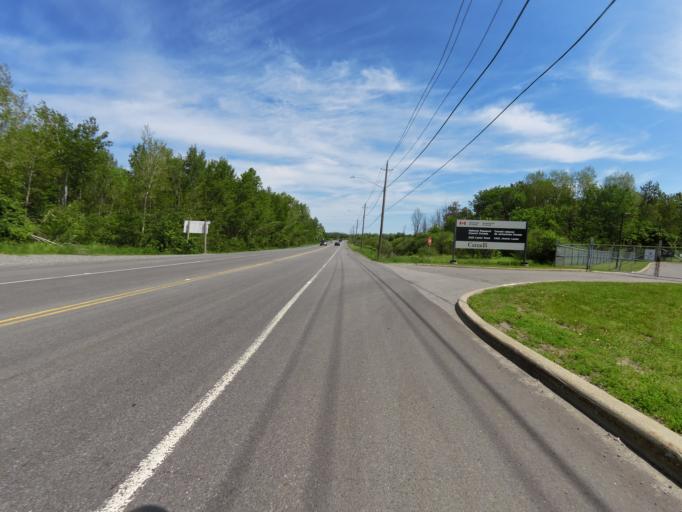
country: CA
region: Ontario
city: Ottawa
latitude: 45.3300
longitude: -75.6488
